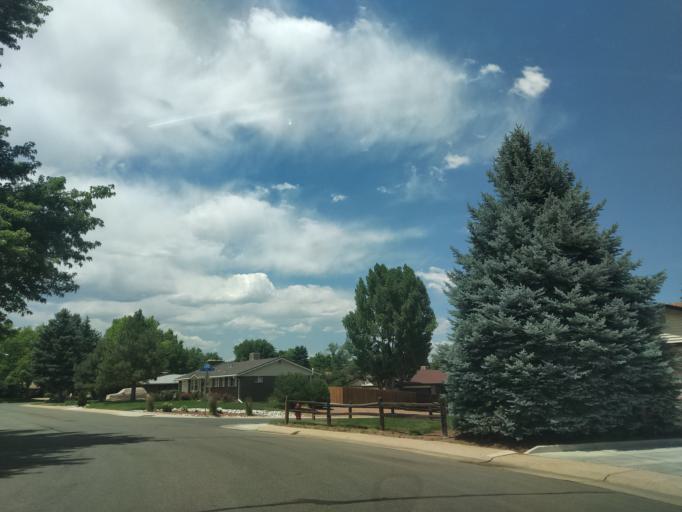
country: US
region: Colorado
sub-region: Jefferson County
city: Lakewood
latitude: 39.6804
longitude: -105.0919
